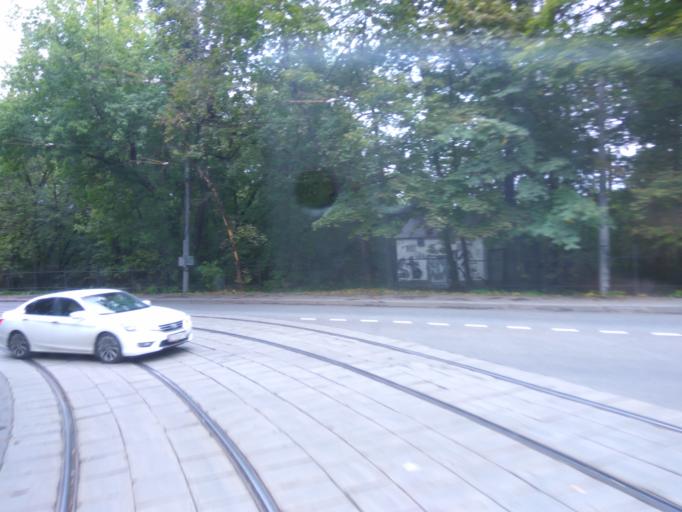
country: RU
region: Moscow
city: Metrogorodok
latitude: 55.7870
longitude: 37.7626
